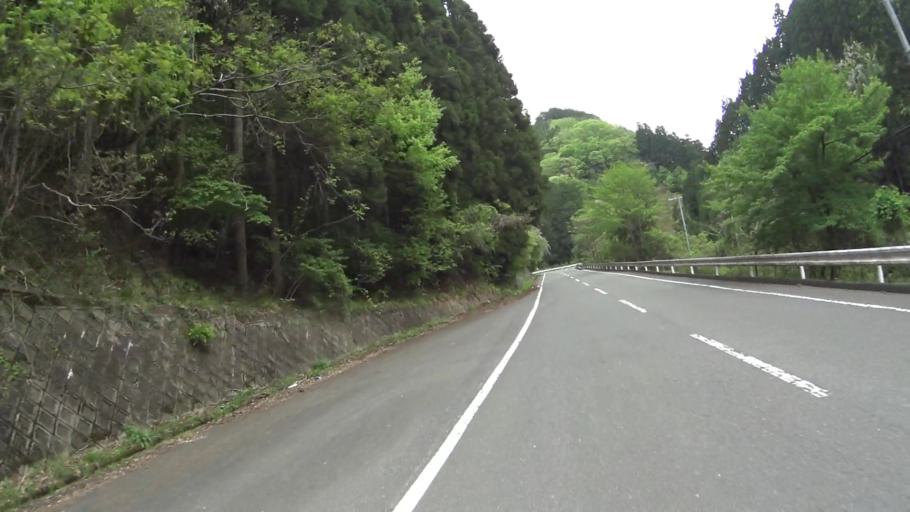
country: JP
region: Kyoto
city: Kameoka
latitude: 35.1336
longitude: 135.6182
